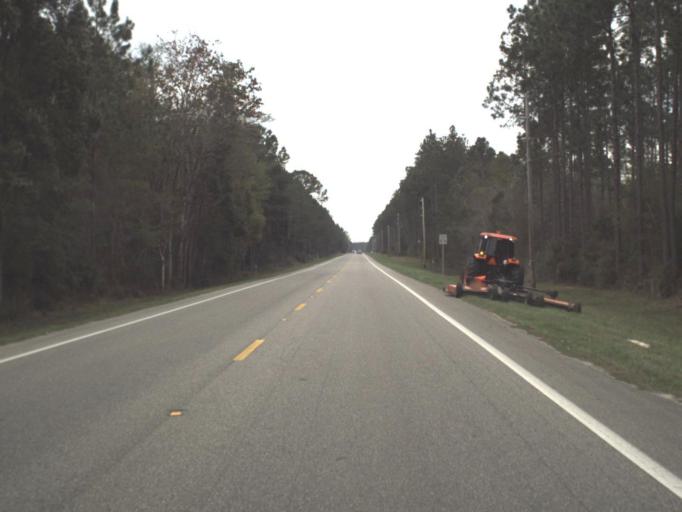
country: US
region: Florida
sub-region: Gulf County
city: Wewahitchka
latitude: 30.1955
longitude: -85.2073
